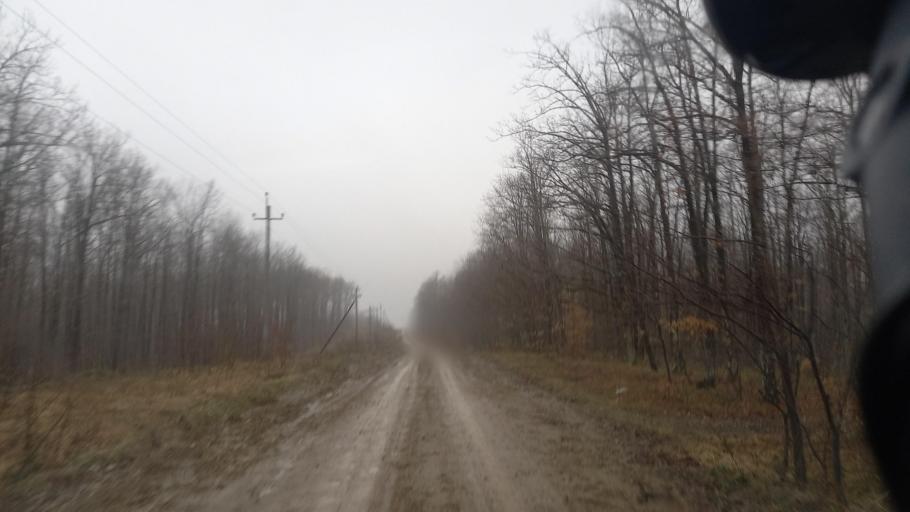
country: RU
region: Krasnodarskiy
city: Saratovskaya
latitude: 44.6167
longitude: 39.2502
